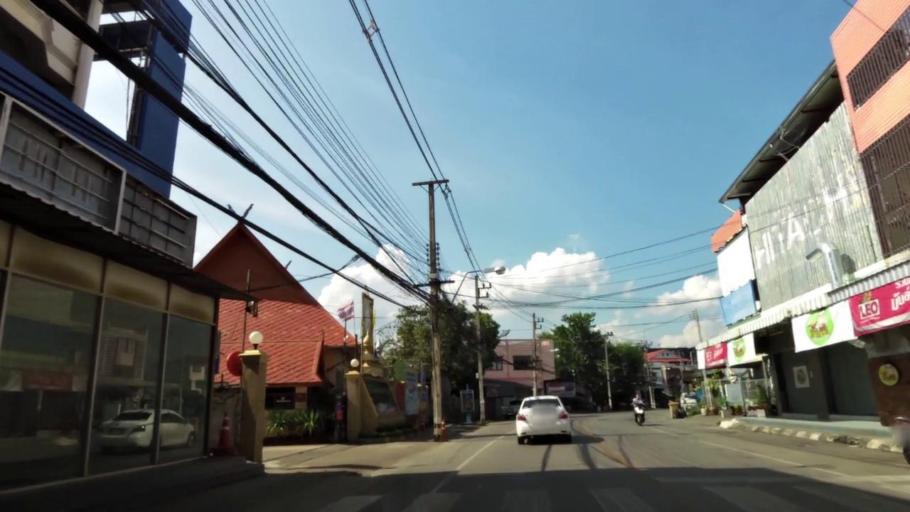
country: TH
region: Phrae
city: Phrae
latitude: 18.1389
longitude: 100.1437
